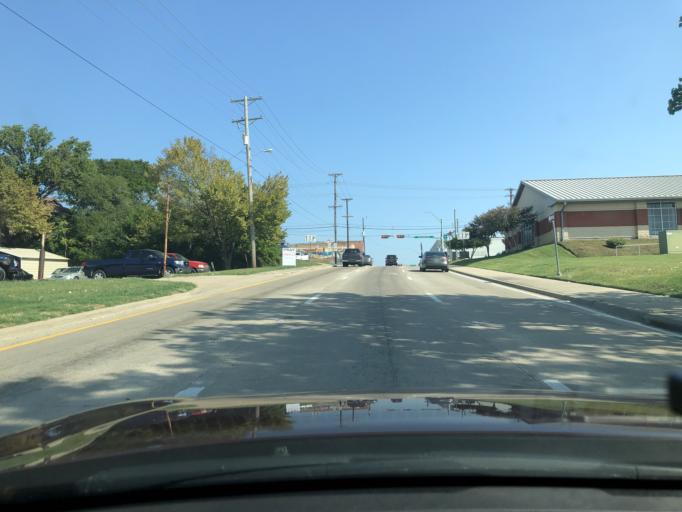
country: US
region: Texas
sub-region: Rockwall County
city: Rockwall
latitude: 32.9295
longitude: -96.4603
